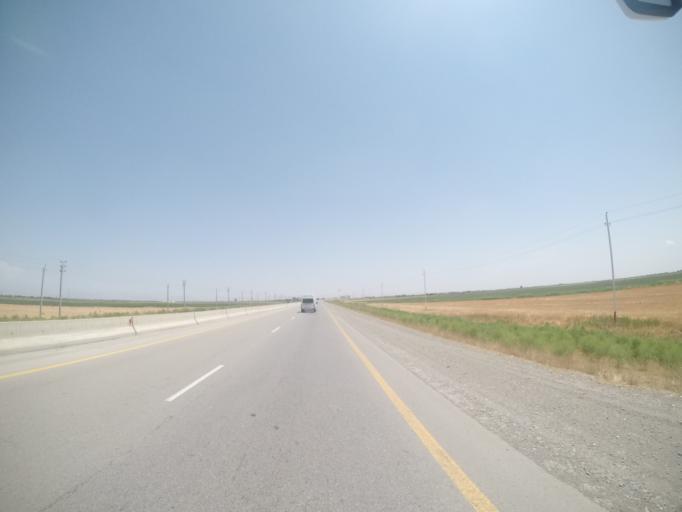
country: AZ
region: Kurdamir Rayon
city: Kyurdarmir
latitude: 40.3170
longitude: 48.1755
